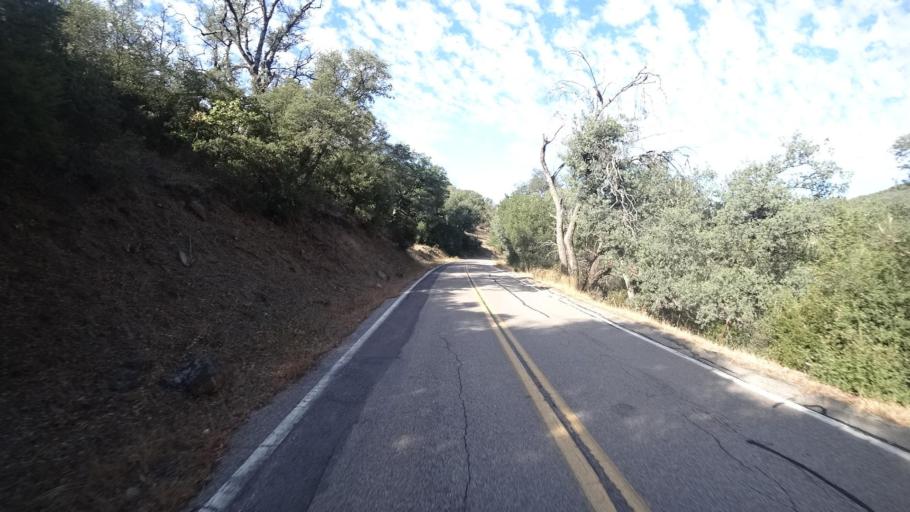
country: US
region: California
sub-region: San Diego County
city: Ramona
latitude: 33.1972
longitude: -116.7684
